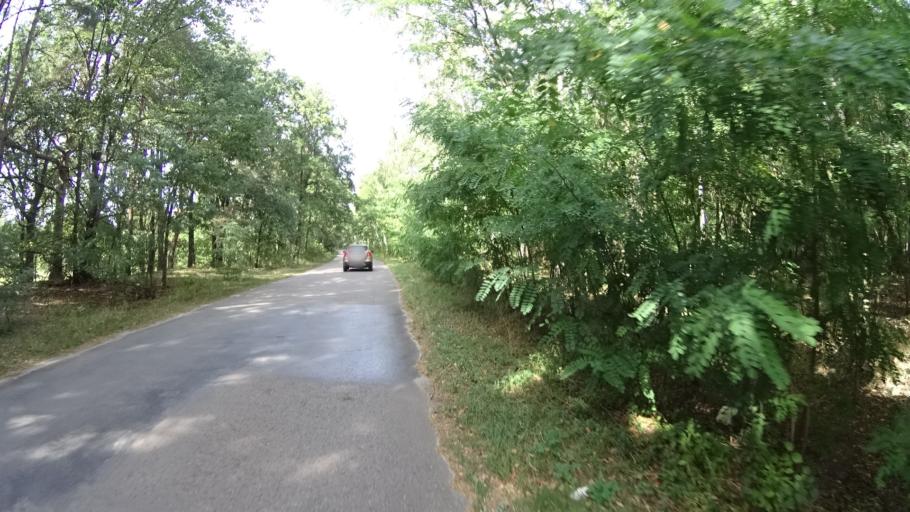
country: PL
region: Masovian Voivodeship
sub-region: Powiat legionowski
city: Serock
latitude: 52.4919
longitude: 21.0867
